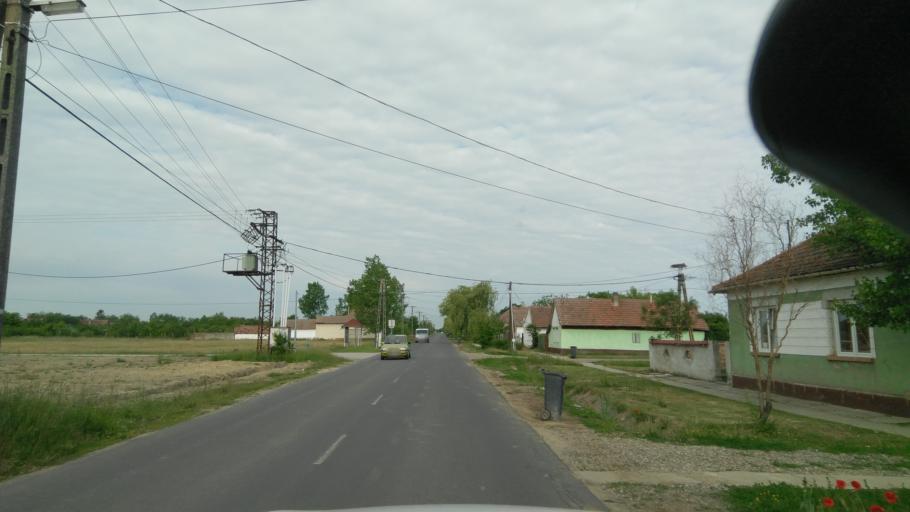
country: HU
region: Bekes
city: Ketegyhaza
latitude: 46.5398
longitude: 21.1630
